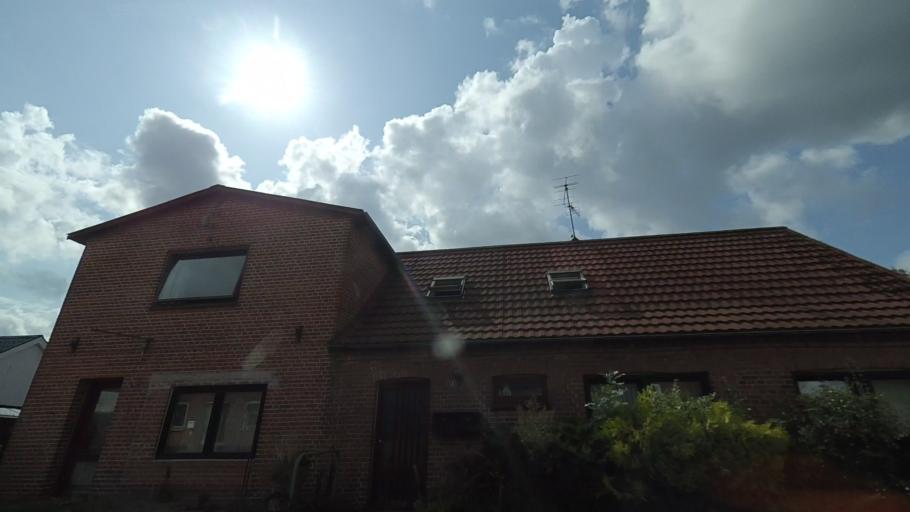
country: DK
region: Central Jutland
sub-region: Norddjurs Kommune
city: Auning
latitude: 56.4829
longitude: 10.4429
